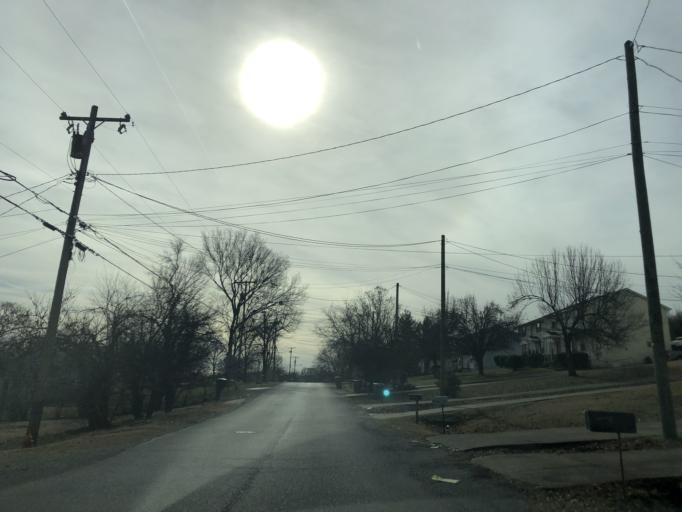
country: US
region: Tennessee
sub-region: Davidson County
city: Nashville
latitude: 36.2211
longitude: -86.7382
